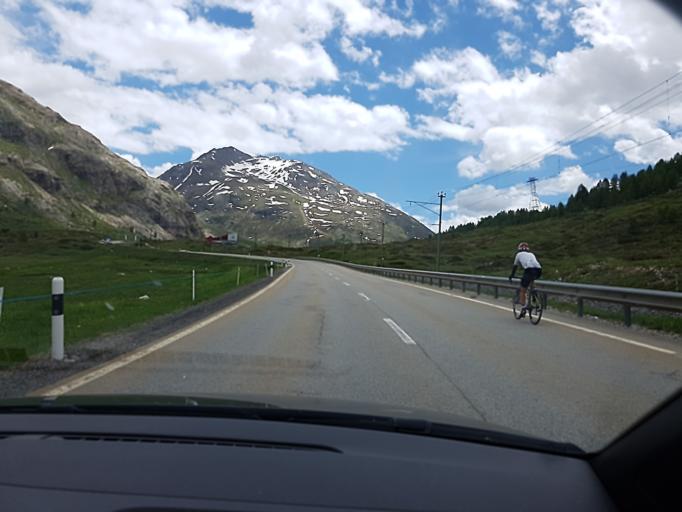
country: CH
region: Grisons
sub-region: Maloja District
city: Pontresina
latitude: 46.4433
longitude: 9.9743
